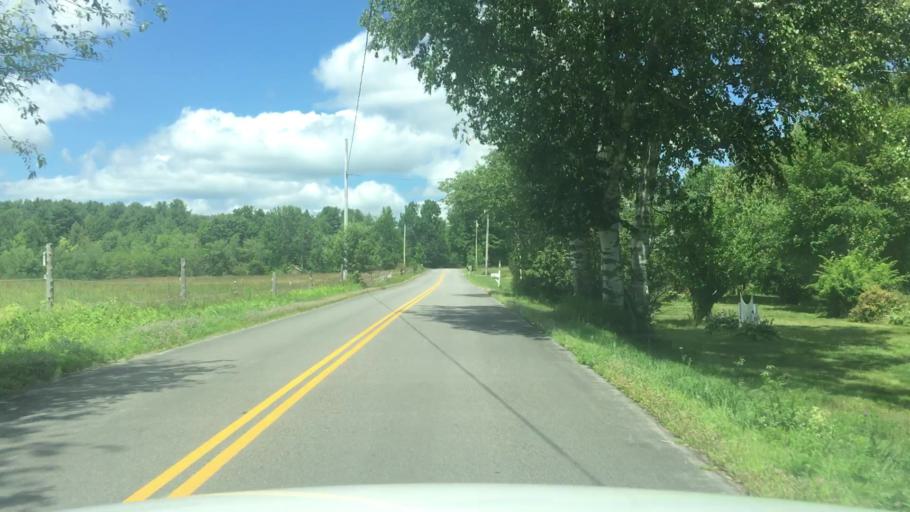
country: US
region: Maine
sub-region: Waldo County
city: Belfast
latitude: 44.4120
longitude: -69.0381
